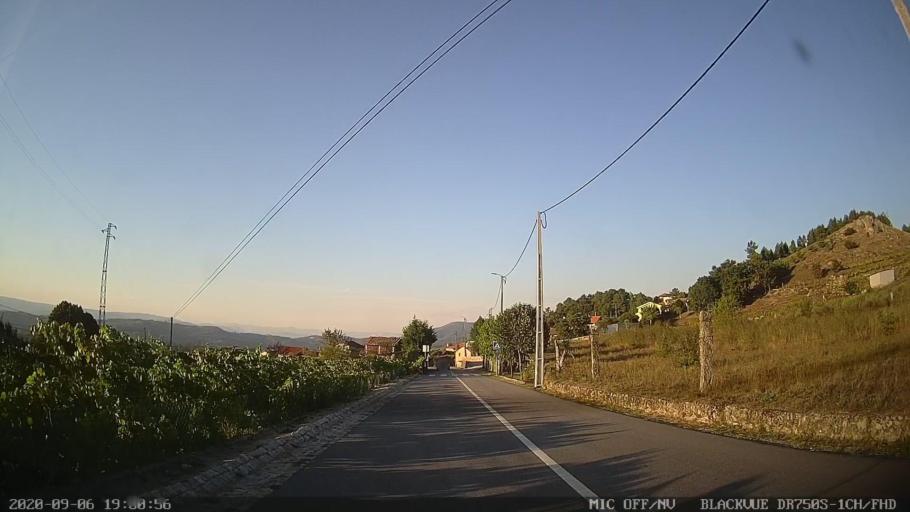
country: PT
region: Porto
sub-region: Baiao
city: Baiao
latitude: 41.2370
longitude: -7.9985
